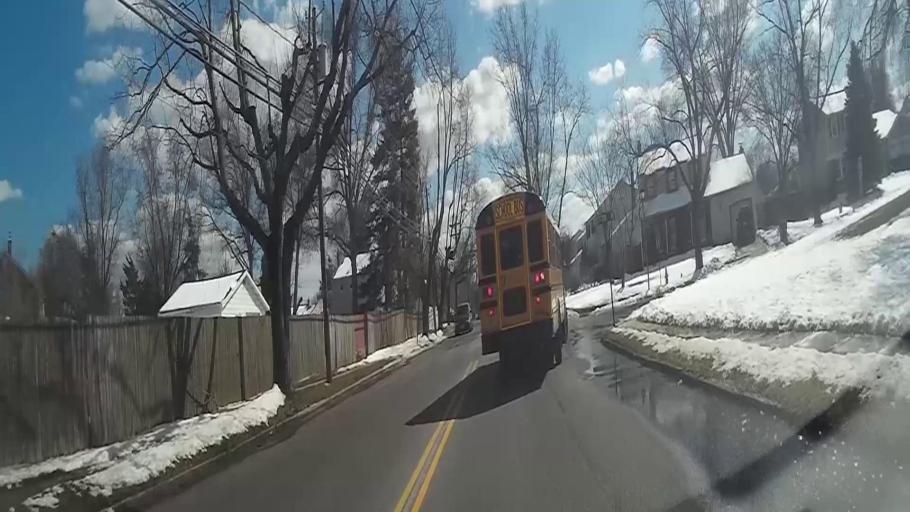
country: US
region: New Jersey
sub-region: Burlington County
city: Marlton
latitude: 39.8768
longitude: -74.9109
